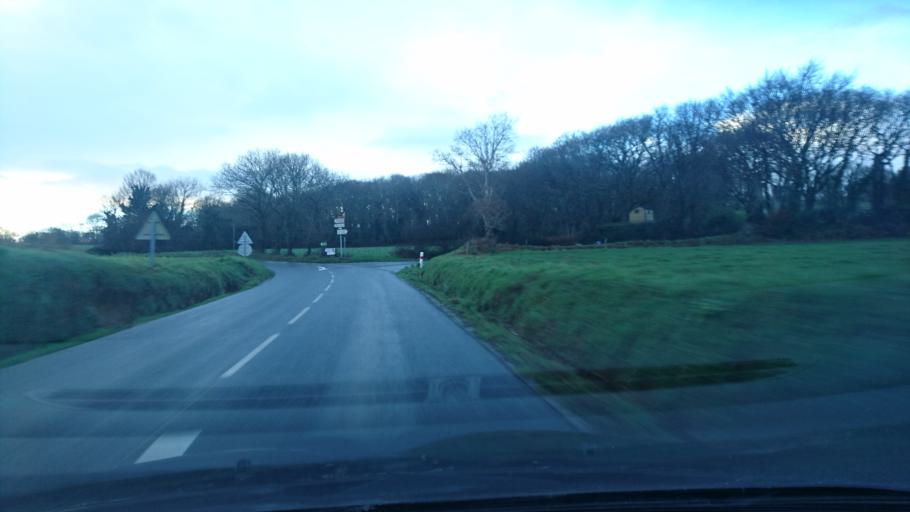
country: FR
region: Brittany
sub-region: Departement du Finistere
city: Guilers
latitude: 48.4047
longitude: -4.5461
